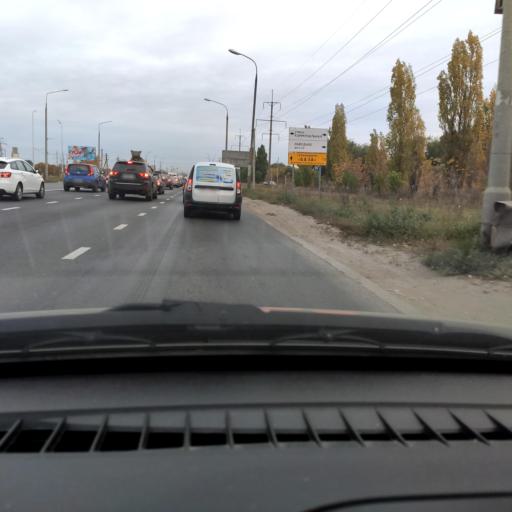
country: RU
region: Samara
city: Tol'yatti
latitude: 53.5595
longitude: 49.2893
